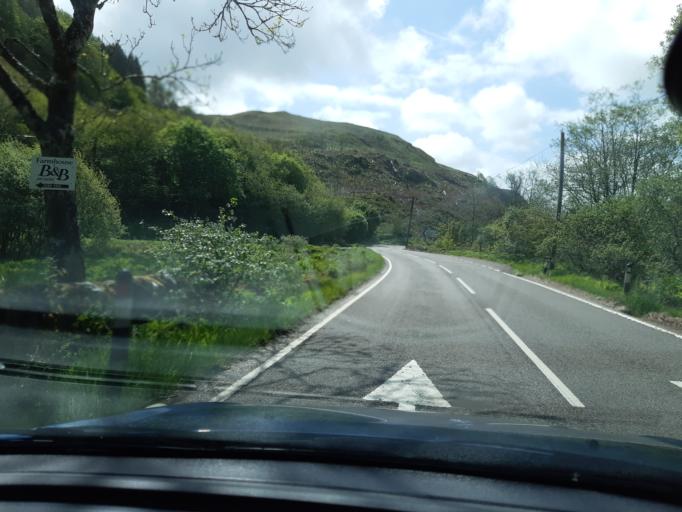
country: GB
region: Scotland
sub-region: Argyll and Bute
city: Lochgilphead
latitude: 56.1519
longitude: -5.4752
